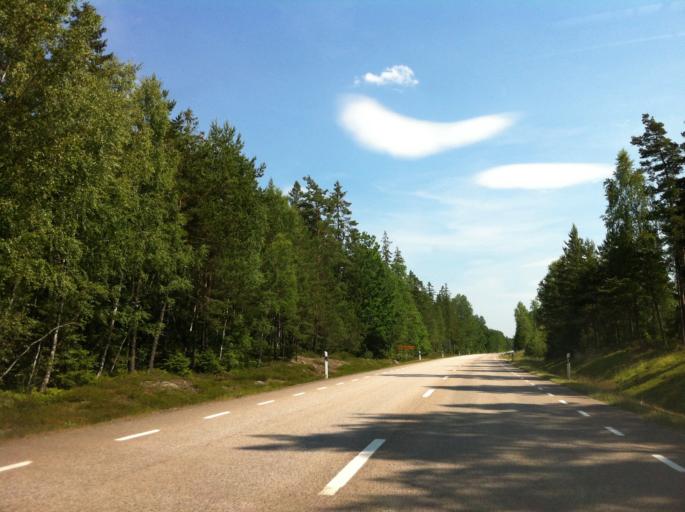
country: SE
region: Kalmar
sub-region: Nybro Kommun
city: Nybro
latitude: 56.8342
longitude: 15.7374
